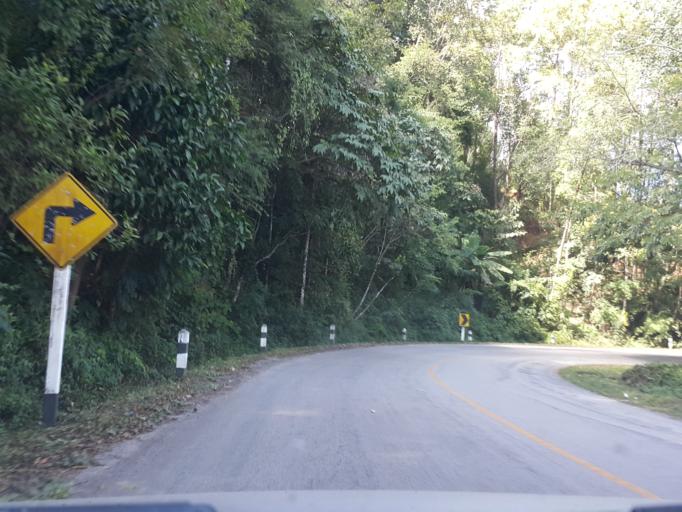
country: TH
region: Mae Hong Son
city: Mae Hi
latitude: 19.2338
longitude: 98.6621
